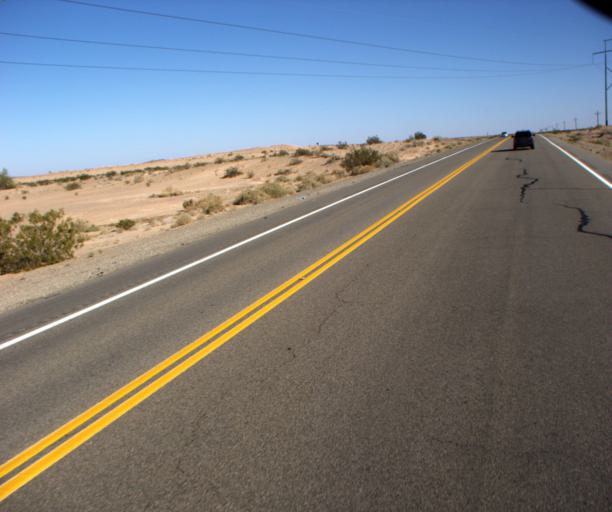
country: US
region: Arizona
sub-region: Yuma County
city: Fortuna Foothills
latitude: 32.8047
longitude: -114.3803
